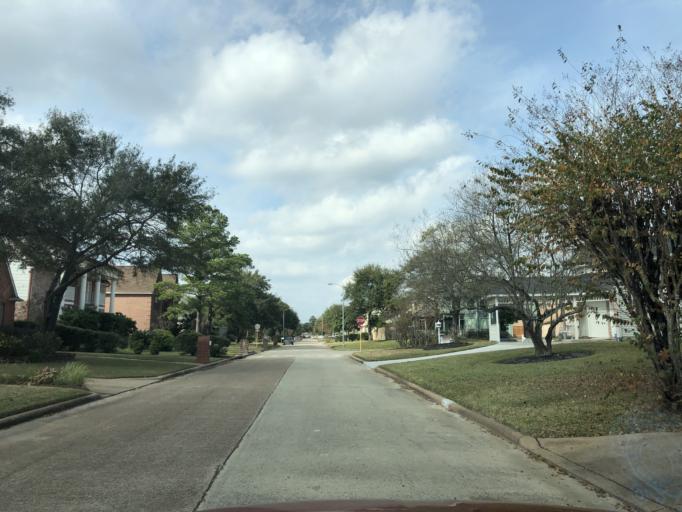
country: US
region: Texas
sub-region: Harris County
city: Tomball
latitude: 30.0320
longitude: -95.5396
